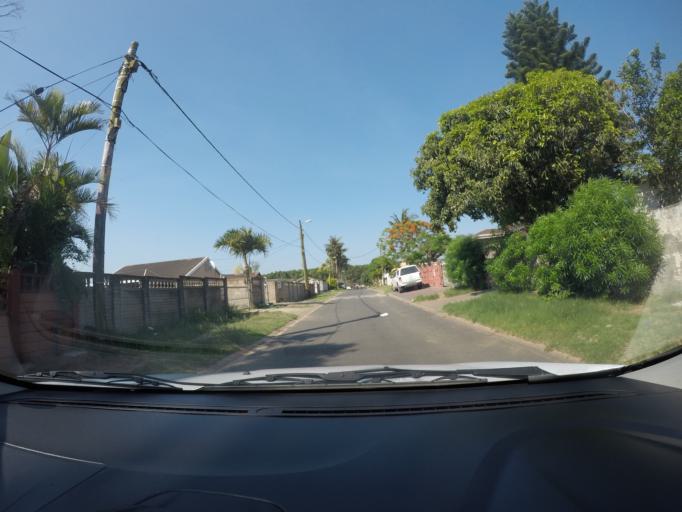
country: ZA
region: KwaZulu-Natal
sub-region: uThungulu District Municipality
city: Richards Bay
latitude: -28.7157
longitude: 32.0417
